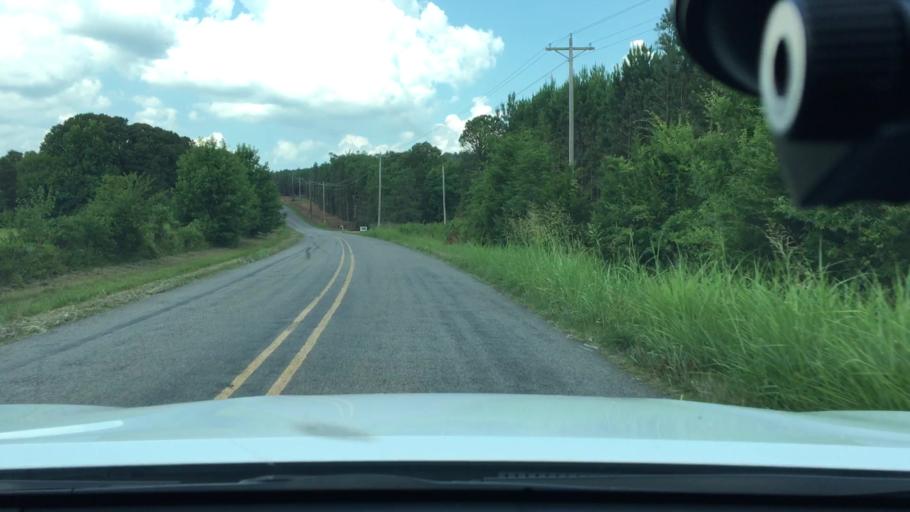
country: US
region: Arkansas
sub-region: Logan County
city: Paris
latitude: 35.2692
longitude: -93.6698
